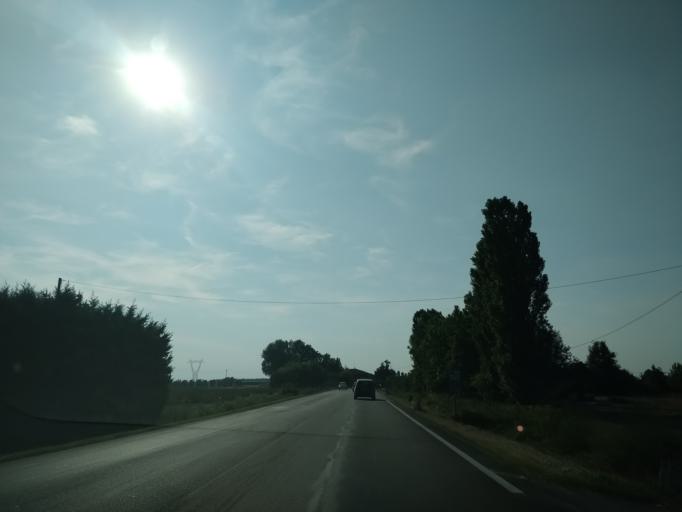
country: IT
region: Emilia-Romagna
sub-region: Provincia di Bologna
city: Castel Maggiore
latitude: 44.6028
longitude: 11.3401
